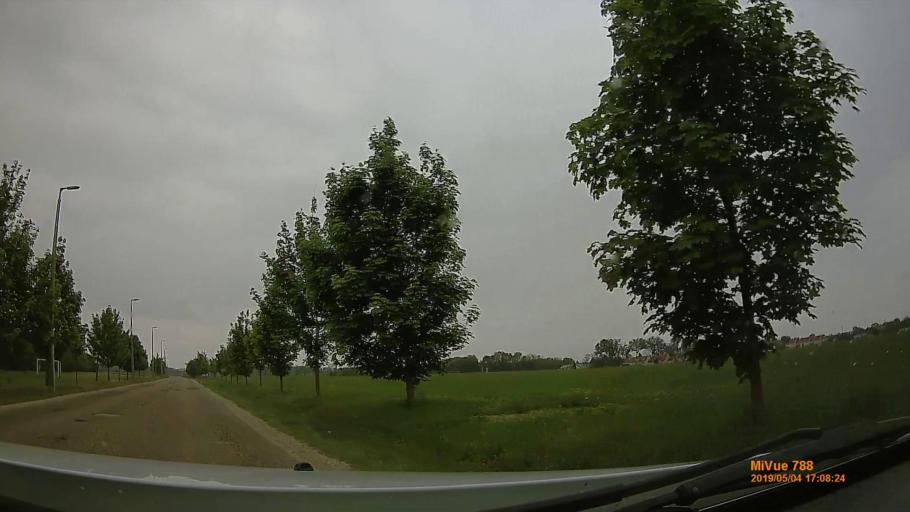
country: HU
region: Gyor-Moson-Sopron
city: Mosonmagyarovar
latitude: 47.8879
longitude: 17.2905
